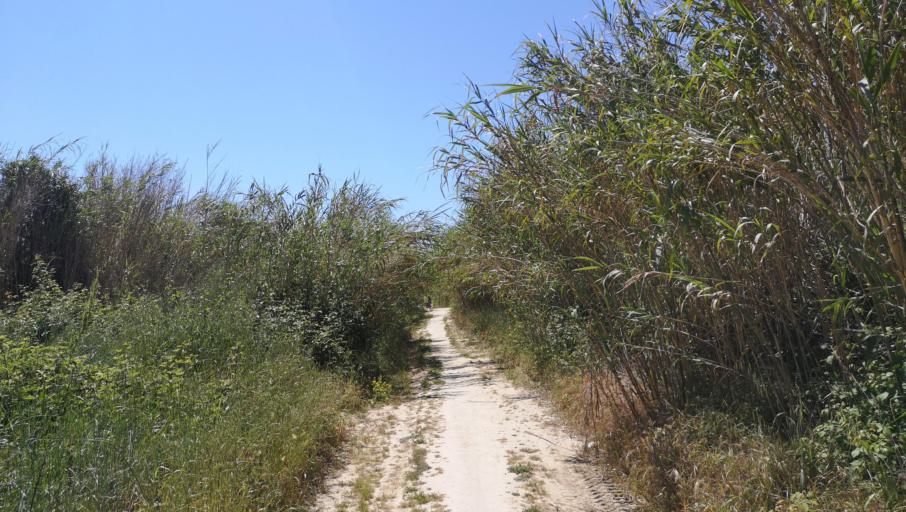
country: IT
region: The Marches
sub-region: Province of Fermo
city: Campofilone
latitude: 43.0636
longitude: 13.8493
